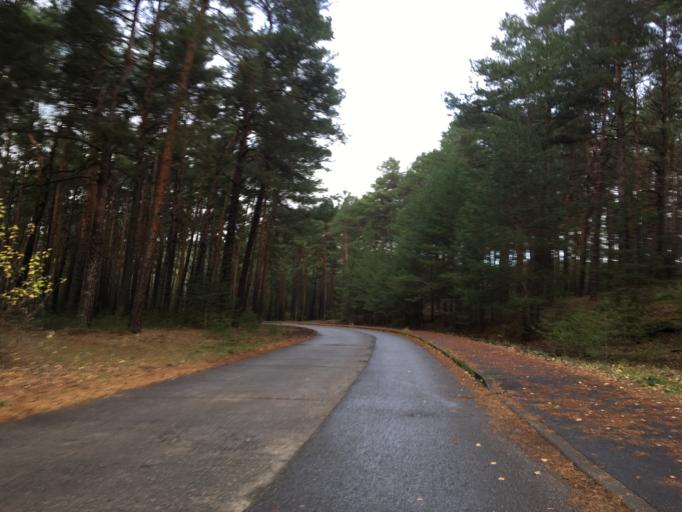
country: DE
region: Brandenburg
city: Schenkendobern
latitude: 51.9668
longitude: 14.5366
